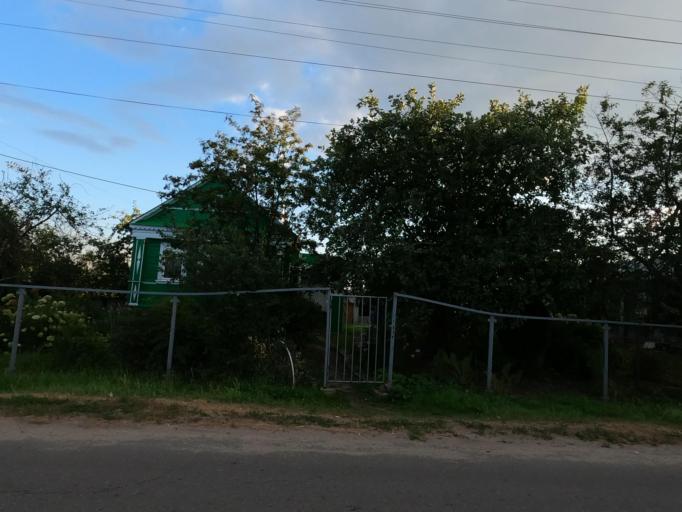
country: RU
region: Moskovskaya
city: Ashitkovo
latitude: 55.4207
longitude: 38.5722
